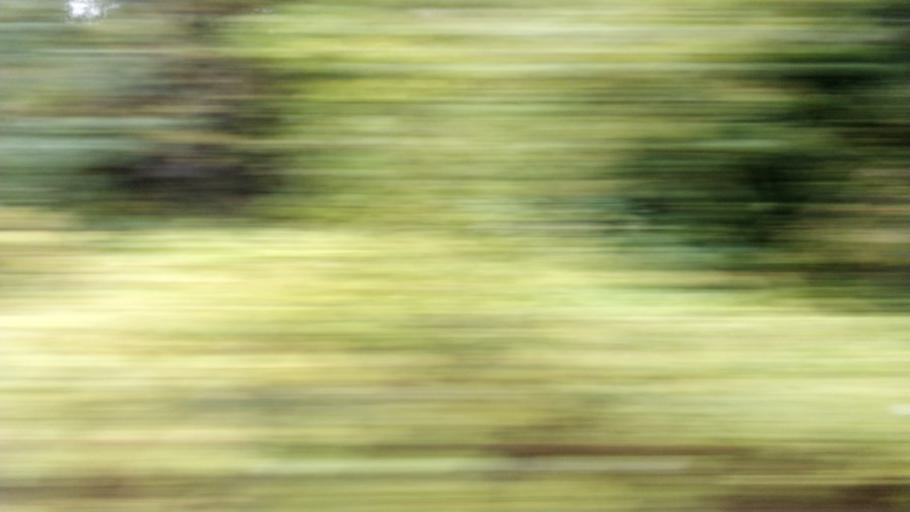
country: GB
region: England
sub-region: Manchester
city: Swinton
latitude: 53.5180
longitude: -2.3614
